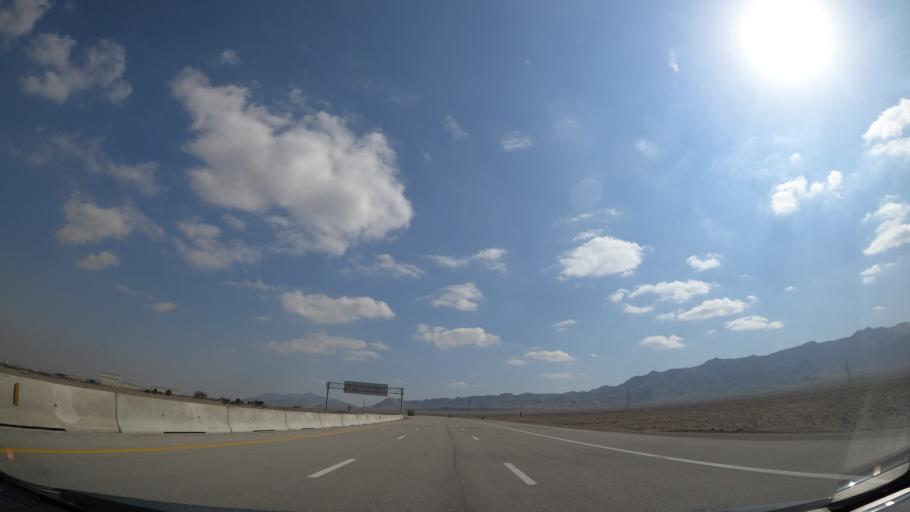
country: IR
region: Alborz
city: Eshtehard
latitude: 35.7196
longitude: 50.5716
